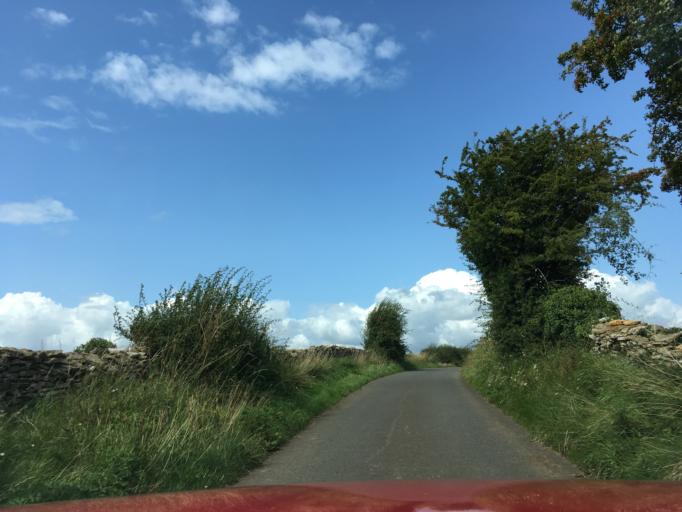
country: GB
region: England
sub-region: Wiltshire
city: Luckington
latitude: 51.6106
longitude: -2.2528
